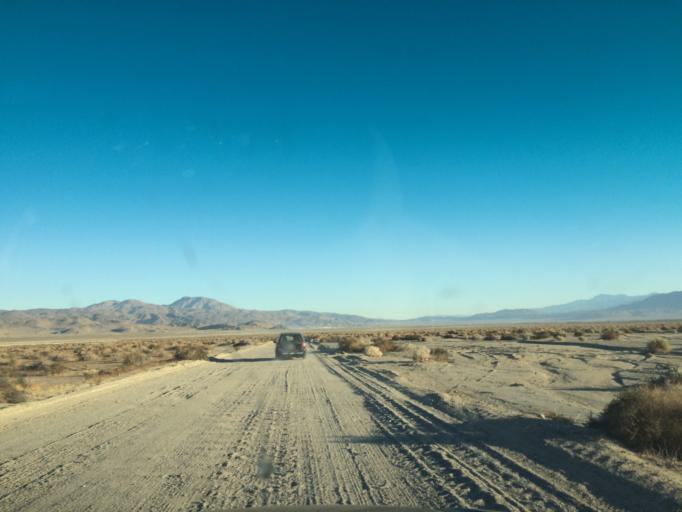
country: US
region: California
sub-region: San Bernardino County
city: Searles Valley
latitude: 35.6397
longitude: -117.3759
